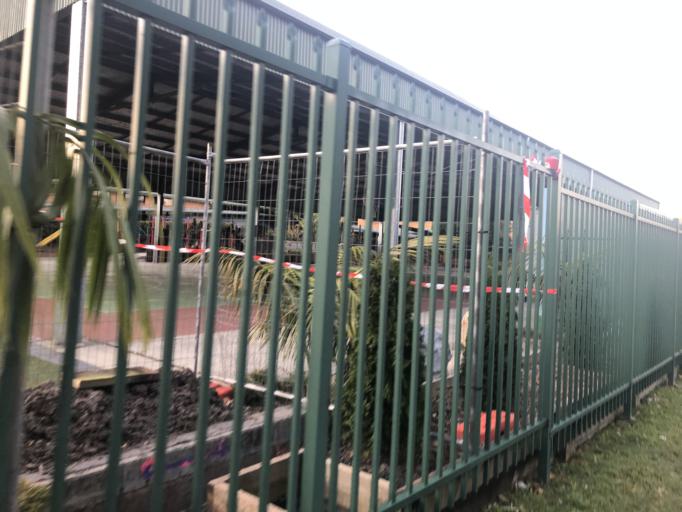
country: AU
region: New South Wales
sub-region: Coffs Harbour
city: Coffs Harbour
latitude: -30.2991
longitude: 153.1206
